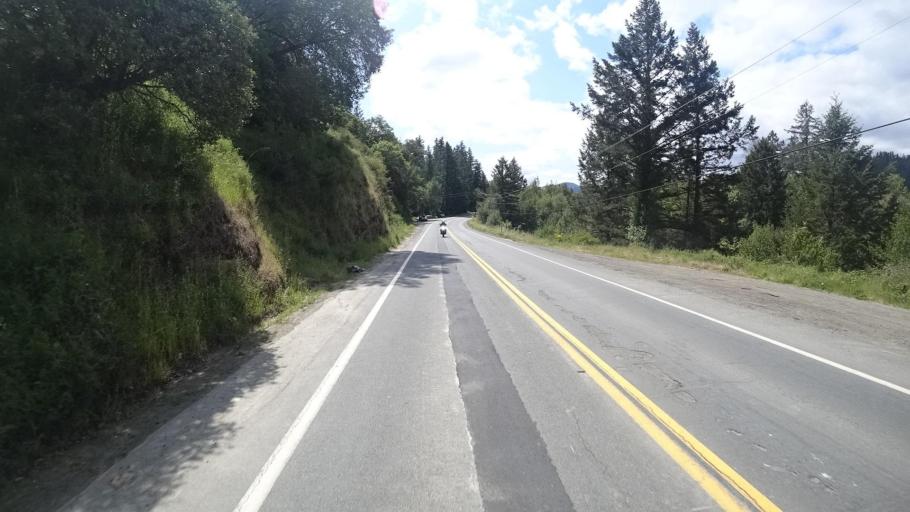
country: US
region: California
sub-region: Humboldt County
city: Redway
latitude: 40.1138
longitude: -123.7946
